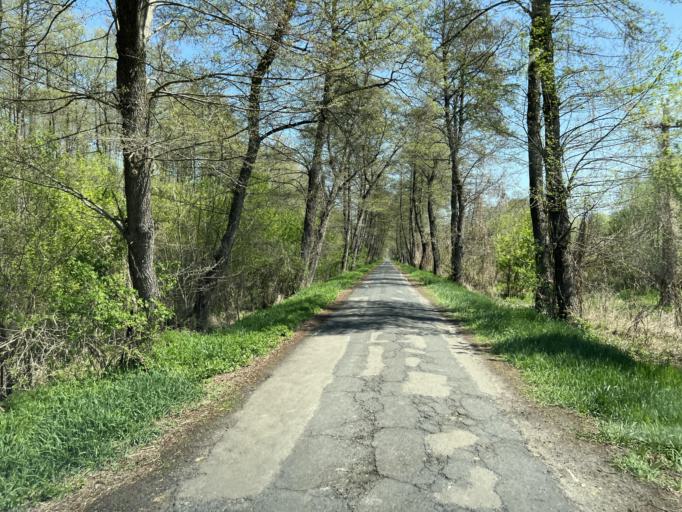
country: HU
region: Pest
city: Inarcs
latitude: 47.2596
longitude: 19.2887
